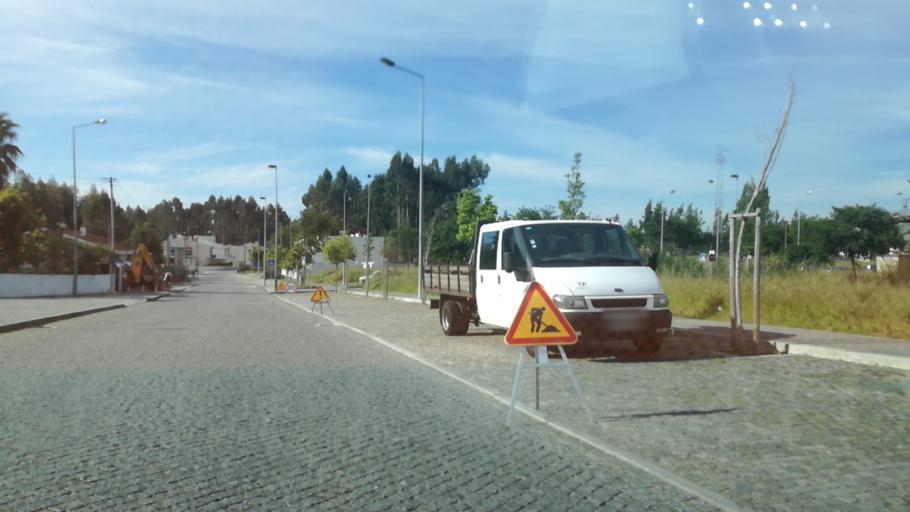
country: PT
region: Porto
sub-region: Maia
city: Nogueira
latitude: 41.2406
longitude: -8.5932
